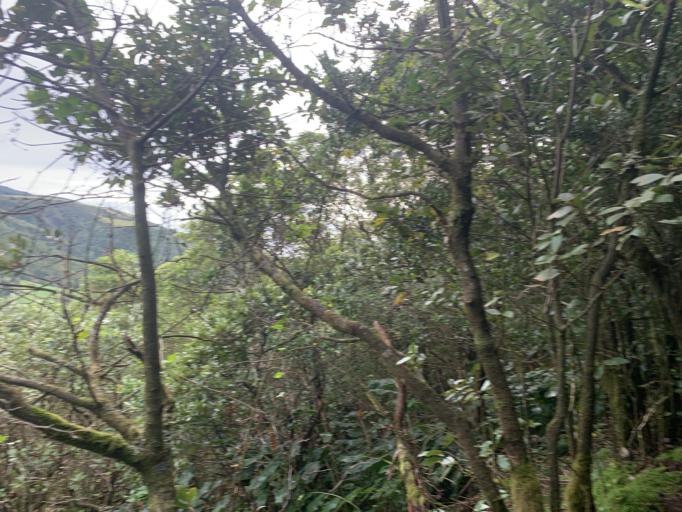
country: PT
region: Azores
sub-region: Vila Franca do Campo
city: Vila Franca do Campo
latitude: 37.7426
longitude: -25.4742
